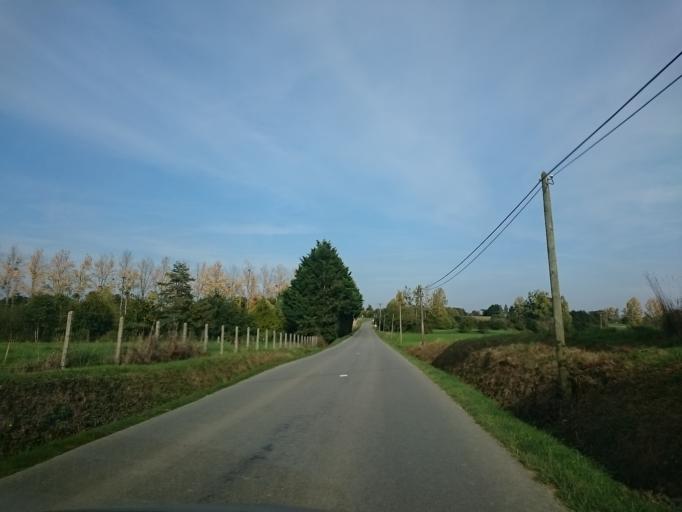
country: FR
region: Brittany
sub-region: Departement d'Ille-et-Vilaine
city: Corps-Nuds
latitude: 47.9493
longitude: -1.5579
